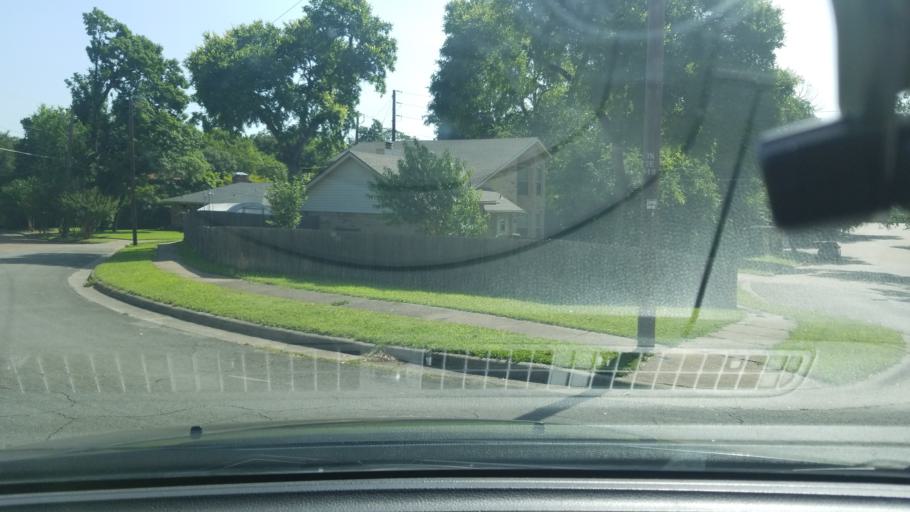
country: US
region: Texas
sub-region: Dallas County
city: Mesquite
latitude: 32.8106
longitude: -96.6914
